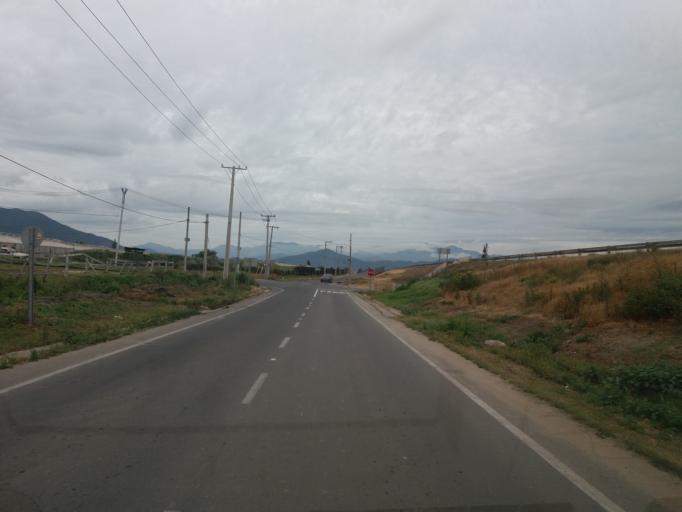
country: CL
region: Valparaiso
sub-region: Provincia de Quillota
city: Quillota
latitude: -32.9183
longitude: -71.2765
